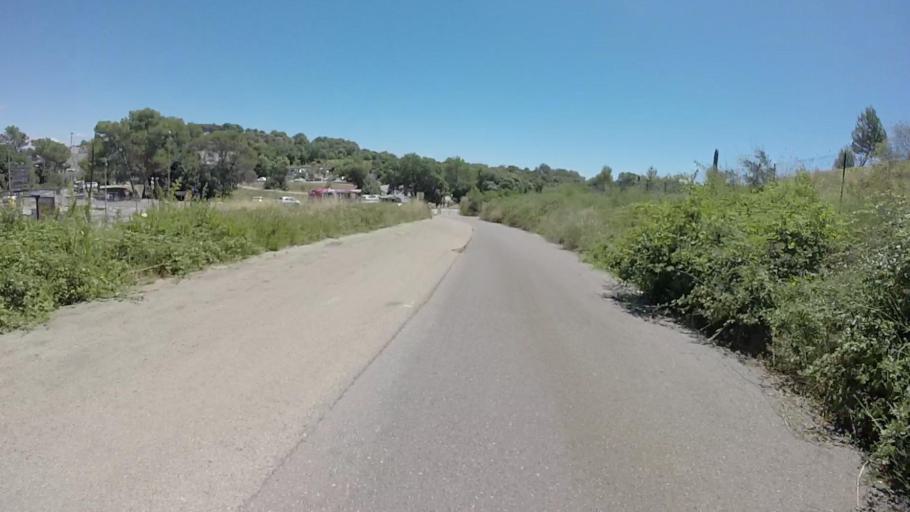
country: FR
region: Provence-Alpes-Cote d'Azur
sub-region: Departement des Alpes-Maritimes
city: Biot
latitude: 43.6167
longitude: 7.0730
